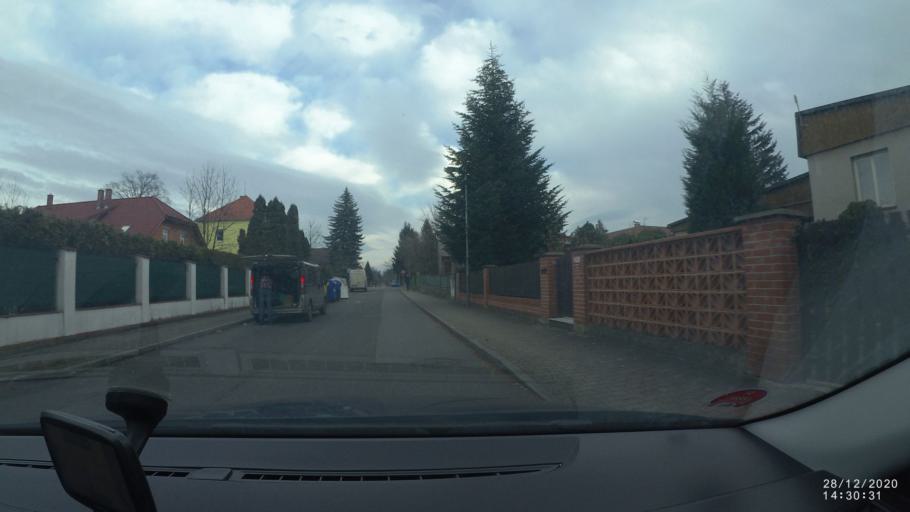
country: CZ
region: Central Bohemia
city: Sestajovice
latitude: 50.0770
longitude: 14.6620
